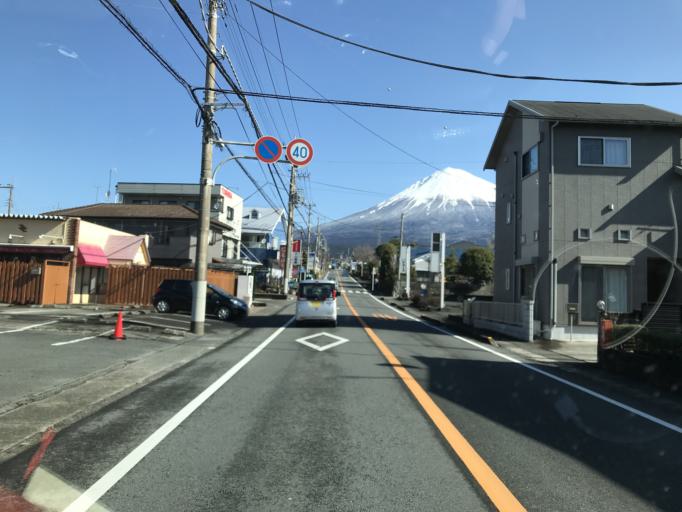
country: JP
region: Shizuoka
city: Fujinomiya
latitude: 35.2494
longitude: 138.6271
